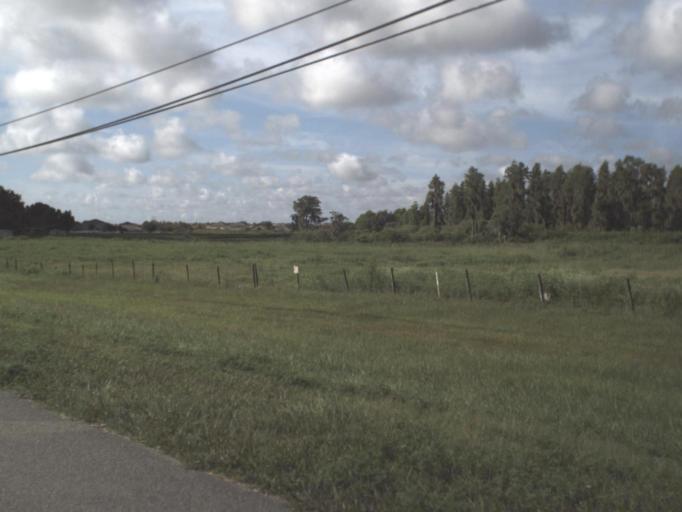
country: US
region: Florida
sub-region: Pasco County
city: Land O' Lakes
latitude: 28.3092
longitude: -82.5034
